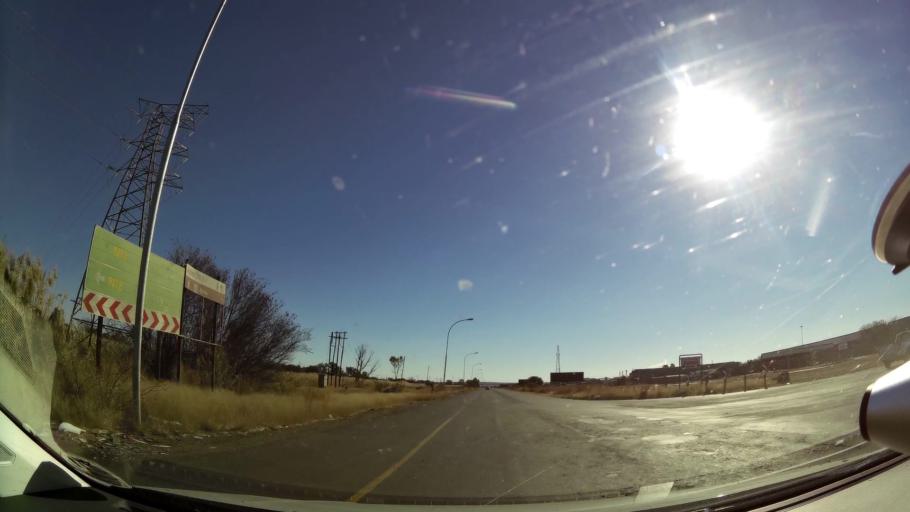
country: ZA
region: Northern Cape
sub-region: Frances Baard District Municipality
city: Kimberley
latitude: -28.7052
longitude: 24.7768
